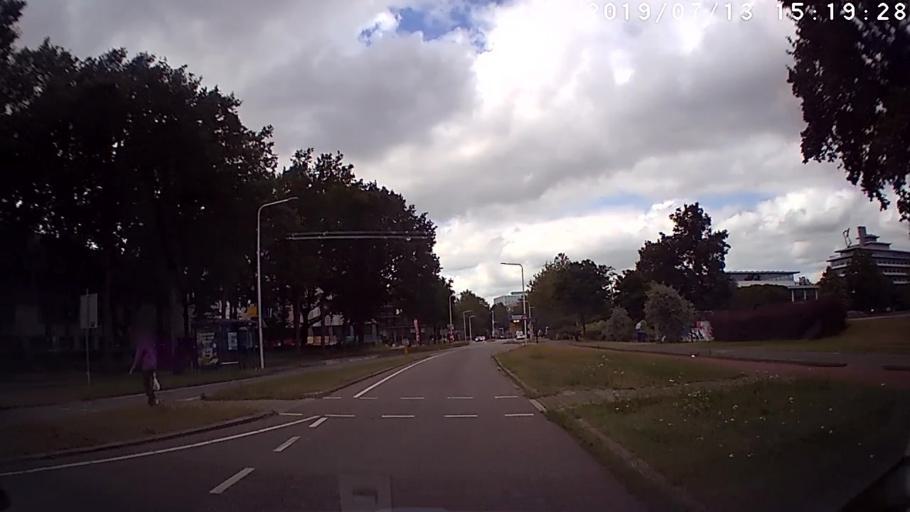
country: NL
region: Overijssel
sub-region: Gemeente Zwolle
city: Zwolle
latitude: 52.5075
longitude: 6.1049
